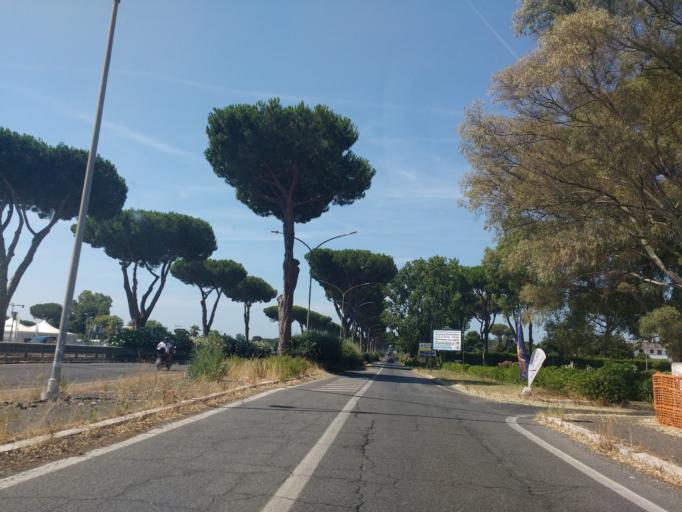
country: IT
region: Latium
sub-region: Citta metropolitana di Roma Capitale
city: Acilia-Castel Fusano-Ostia Antica
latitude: 41.7403
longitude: 12.3505
